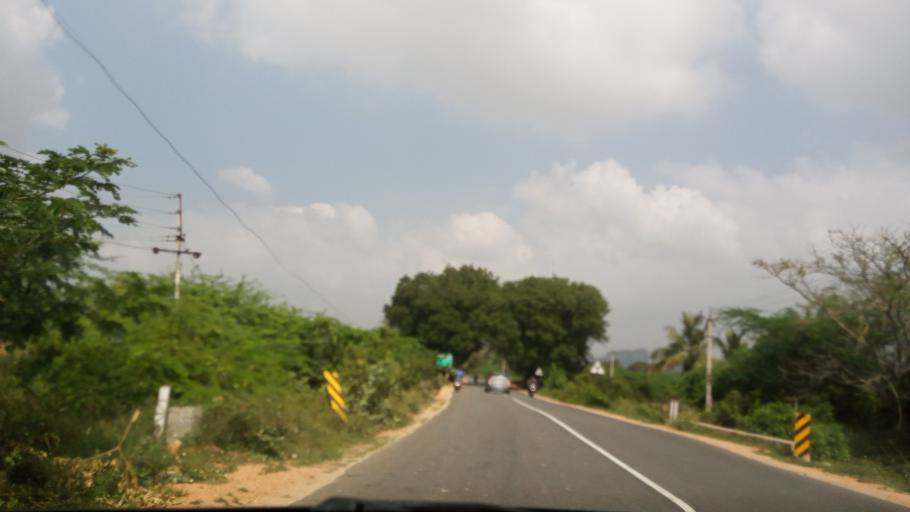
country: IN
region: Andhra Pradesh
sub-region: Chittoor
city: Madanapalle
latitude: 13.6311
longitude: 78.5539
